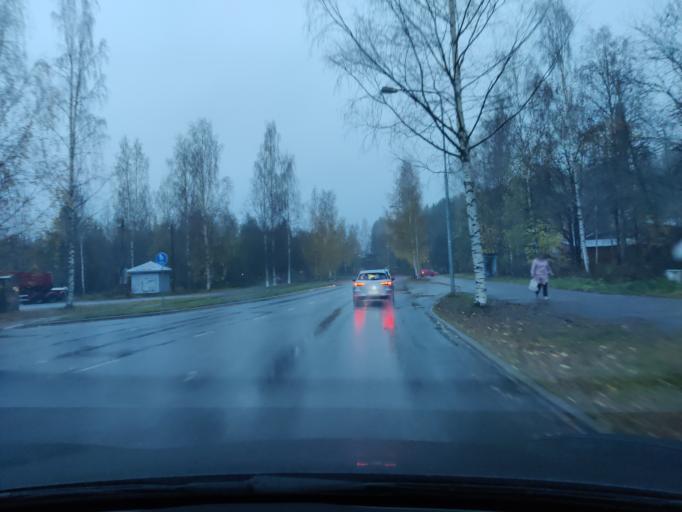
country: FI
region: Northern Savo
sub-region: Kuopio
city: Kuopio
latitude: 62.8500
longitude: 27.6407
